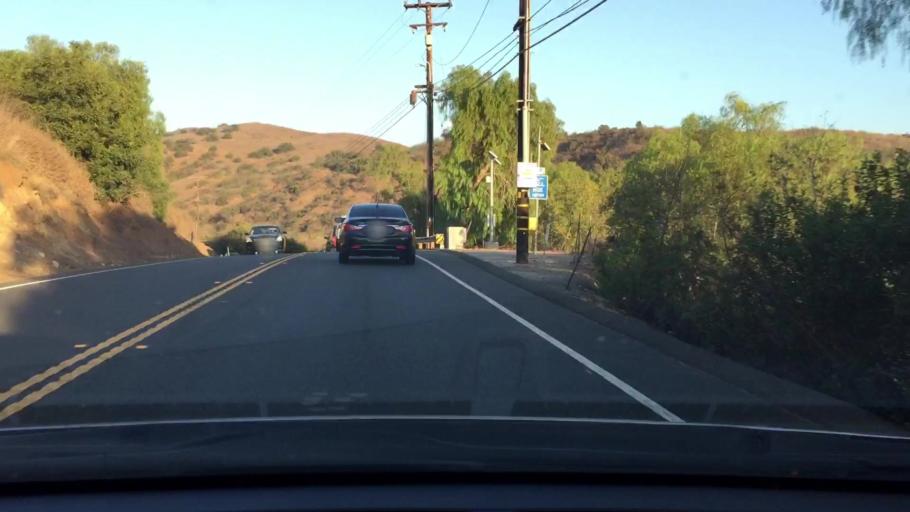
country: US
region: California
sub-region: Orange County
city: Yorba Linda
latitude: 33.9201
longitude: -117.8251
